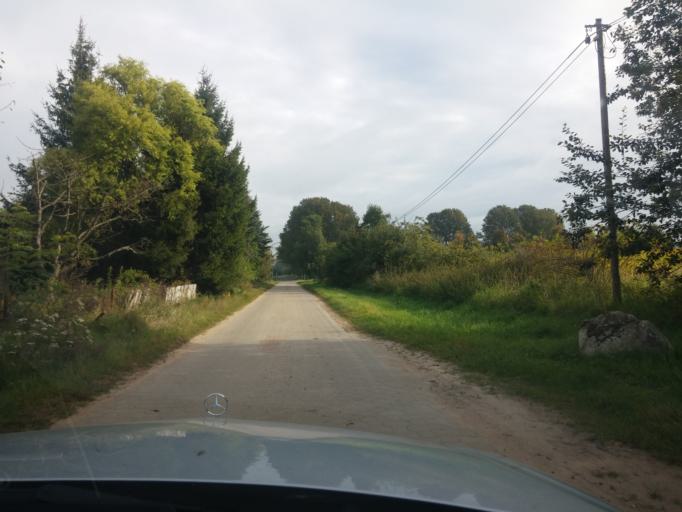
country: DE
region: Brandenburg
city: Putlitz
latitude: 53.3042
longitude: 12.0342
